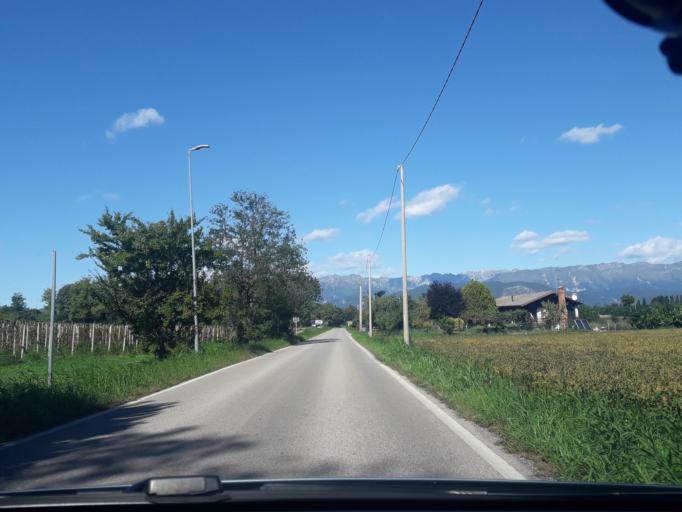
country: IT
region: Friuli Venezia Giulia
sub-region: Provincia di Udine
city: Reana del Roiale
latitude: 46.1335
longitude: 13.2162
